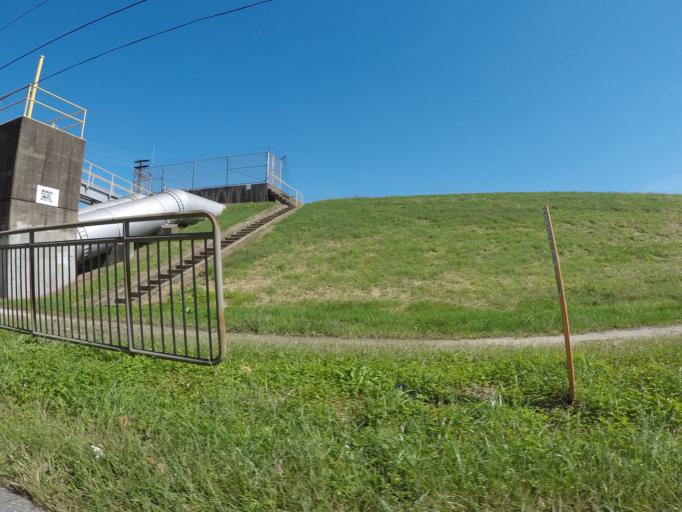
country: US
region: West Virginia
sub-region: Cabell County
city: Huntington
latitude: 38.4174
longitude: -82.3892
